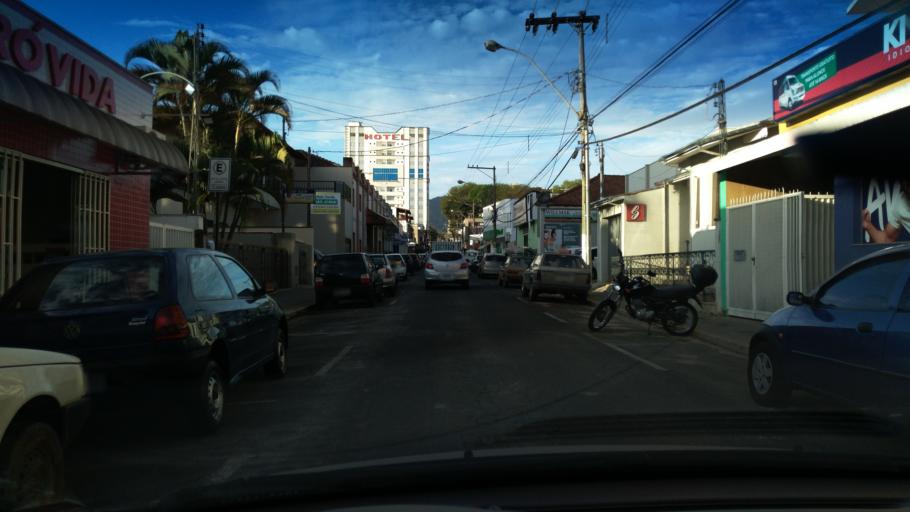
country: BR
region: Minas Gerais
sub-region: Andradas
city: Andradas
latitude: -22.0738
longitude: -46.5765
